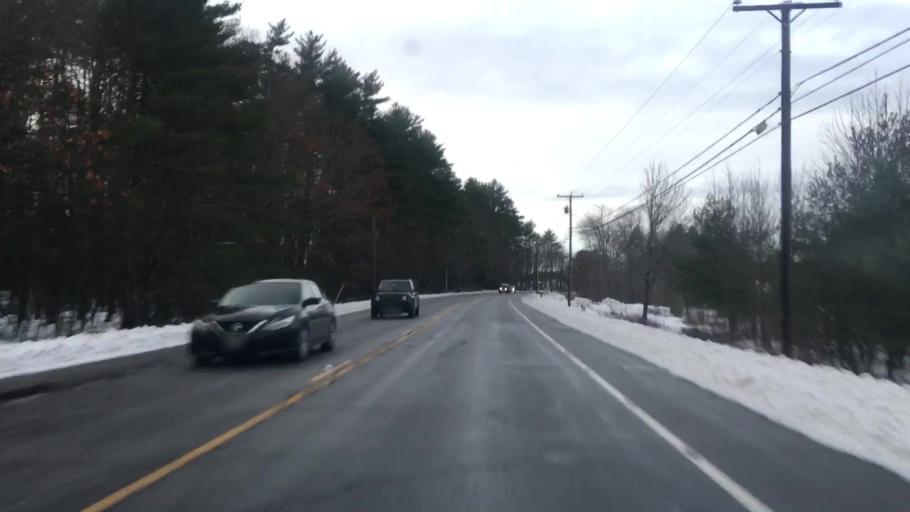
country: US
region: Maine
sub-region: Cumberland County
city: Steep Falls
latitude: 43.7349
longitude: -70.6453
